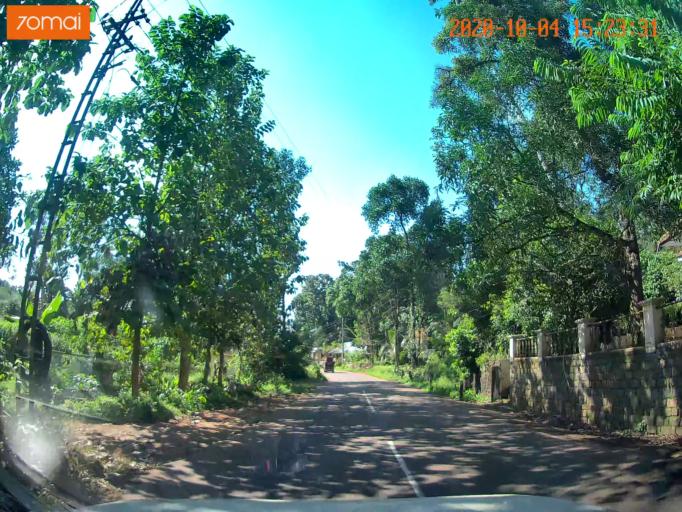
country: IN
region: Kerala
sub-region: Kottayam
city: Palackattumala
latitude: 9.7177
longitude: 76.6591
